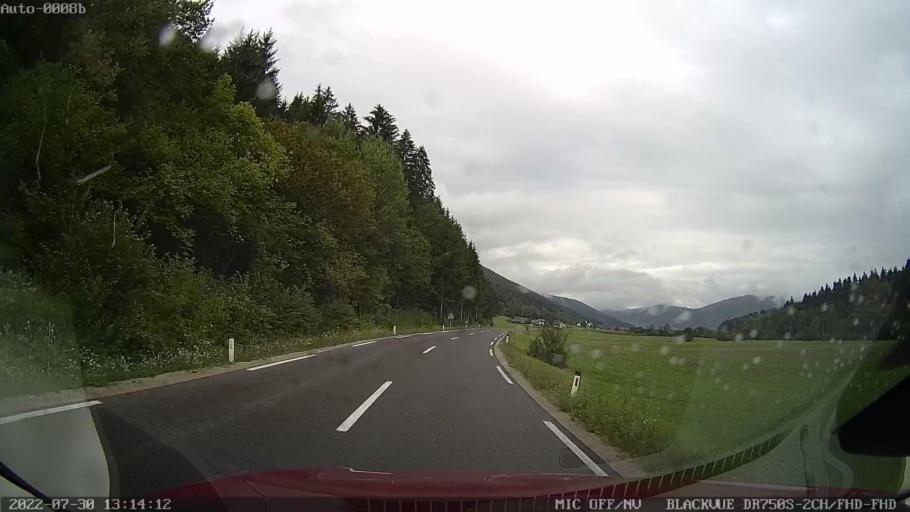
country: SI
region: Dolenjske Toplice
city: Dolenjske Toplice
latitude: 45.7284
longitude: 15.0502
